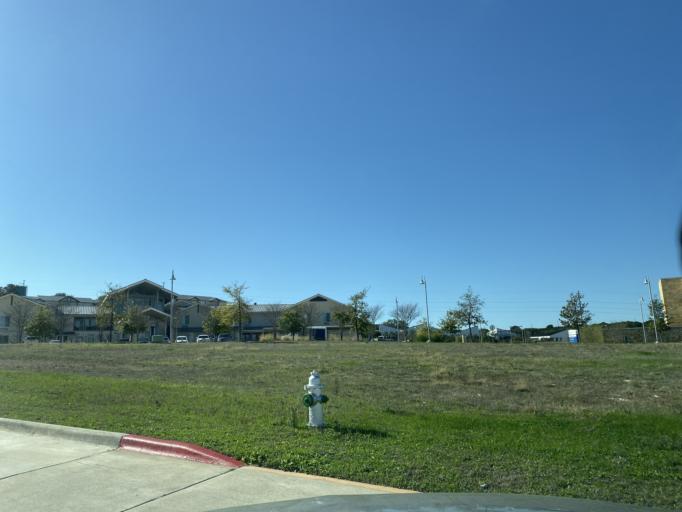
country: US
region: Texas
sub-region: Travis County
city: The Hills
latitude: 30.3318
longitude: -97.9703
